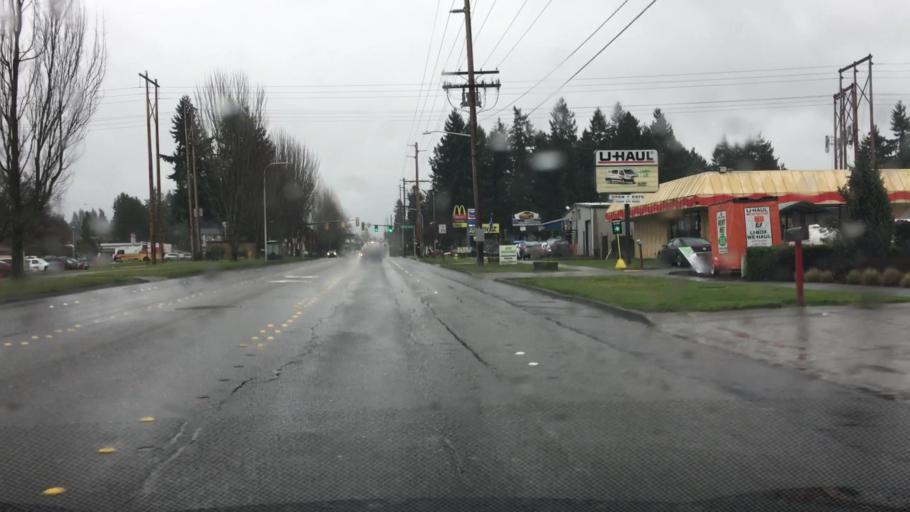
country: US
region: Washington
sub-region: King County
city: Renton
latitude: 47.4886
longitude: -122.1773
